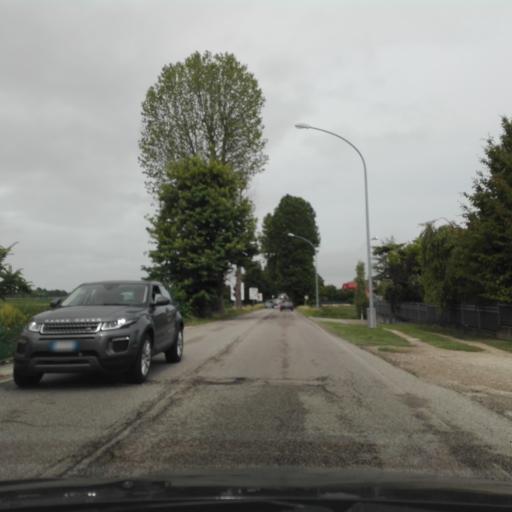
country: IT
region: Veneto
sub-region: Provincia di Rovigo
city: Rovigo
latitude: 45.0757
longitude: 11.7717
